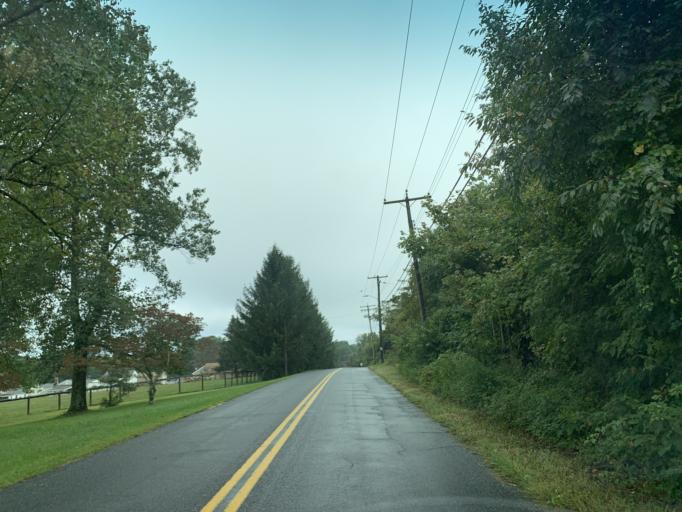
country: US
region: Maryland
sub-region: Harford County
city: Aberdeen
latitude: 39.5678
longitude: -76.1490
